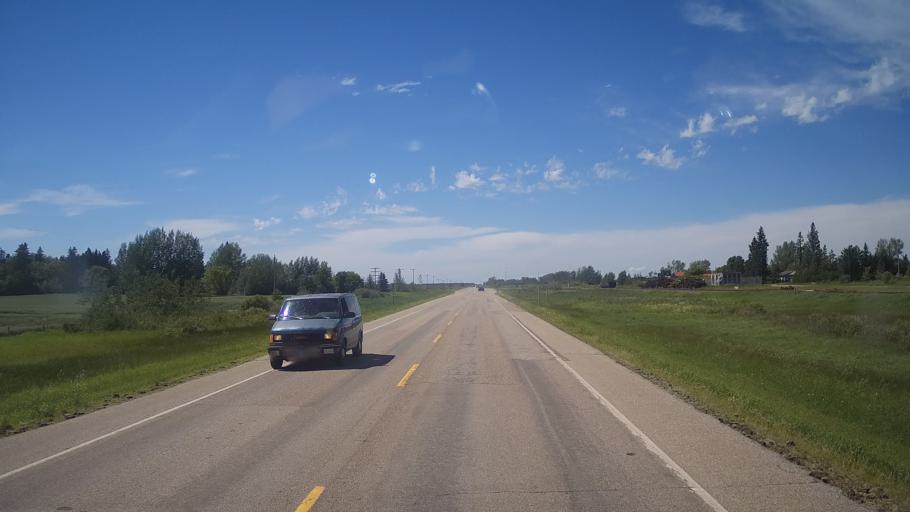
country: CA
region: Saskatchewan
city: Langenburg
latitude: 50.7992
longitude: -101.5734
